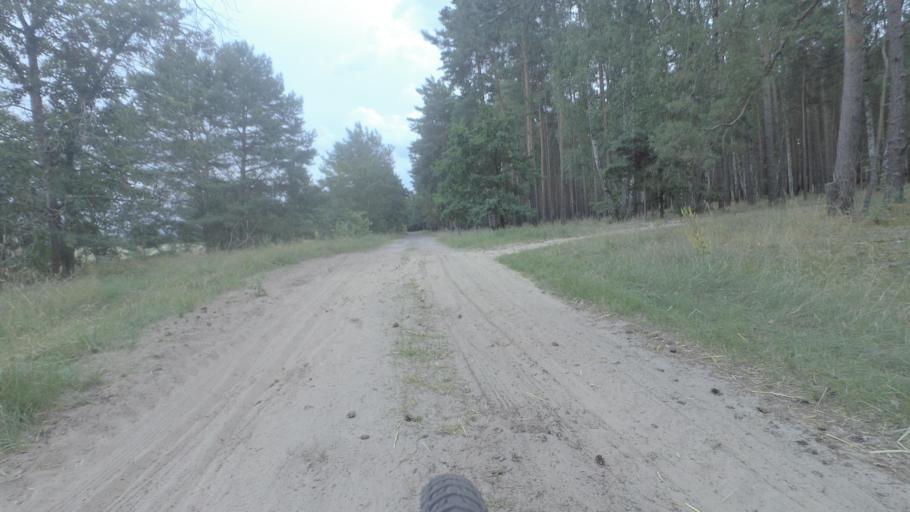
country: DE
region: Brandenburg
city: Rangsdorf
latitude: 52.2661
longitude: 13.3936
